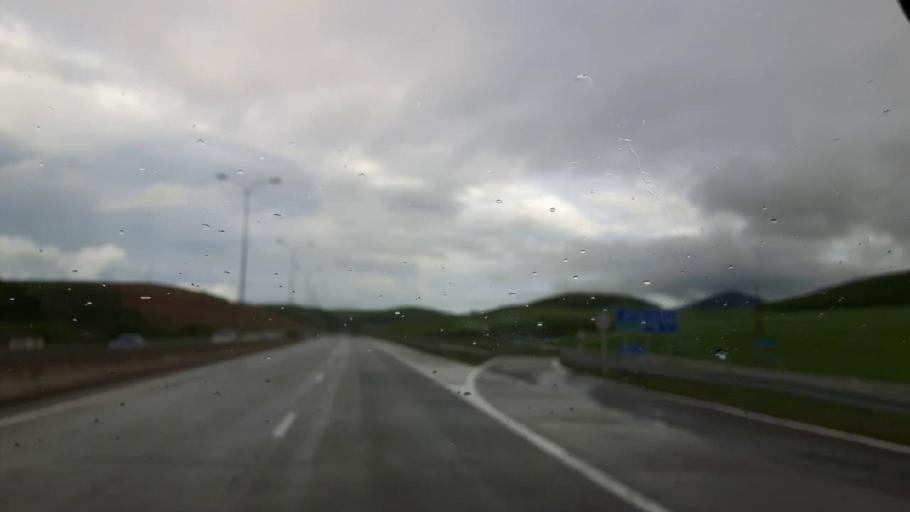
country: GE
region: Shida Kartli
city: Kaspi
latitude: 41.9998
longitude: 44.3893
